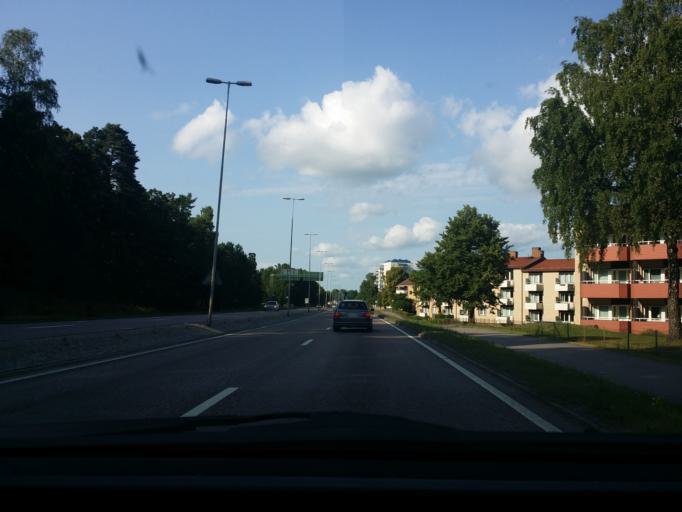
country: SE
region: Vaestmanland
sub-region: Vasteras
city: Vasteras
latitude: 59.6262
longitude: 16.5508
